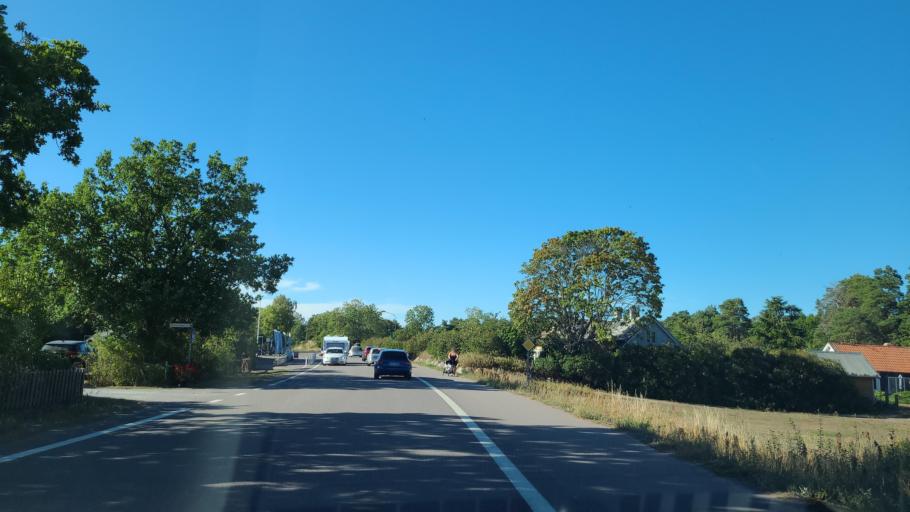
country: SE
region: Kalmar
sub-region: Borgholms Kommun
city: Borgholm
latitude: 57.2491
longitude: 17.0576
